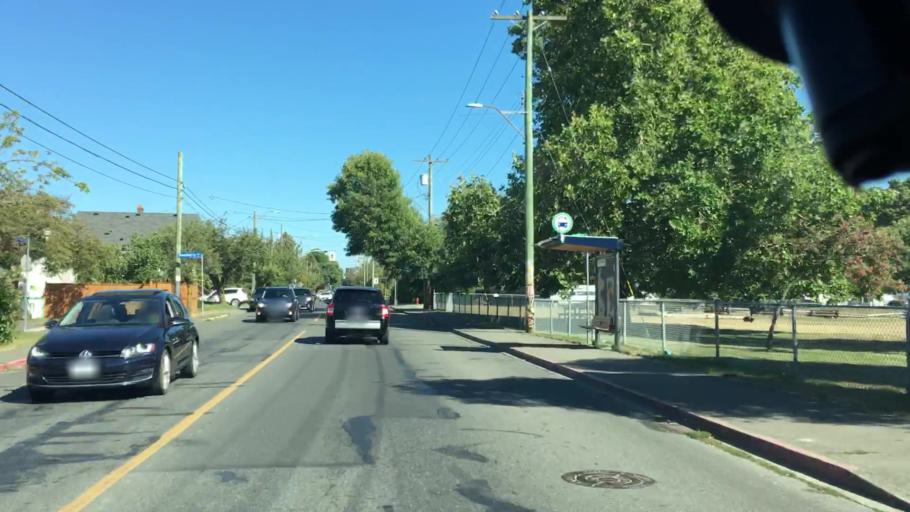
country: CA
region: British Columbia
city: Victoria
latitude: 48.4344
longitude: -123.3441
